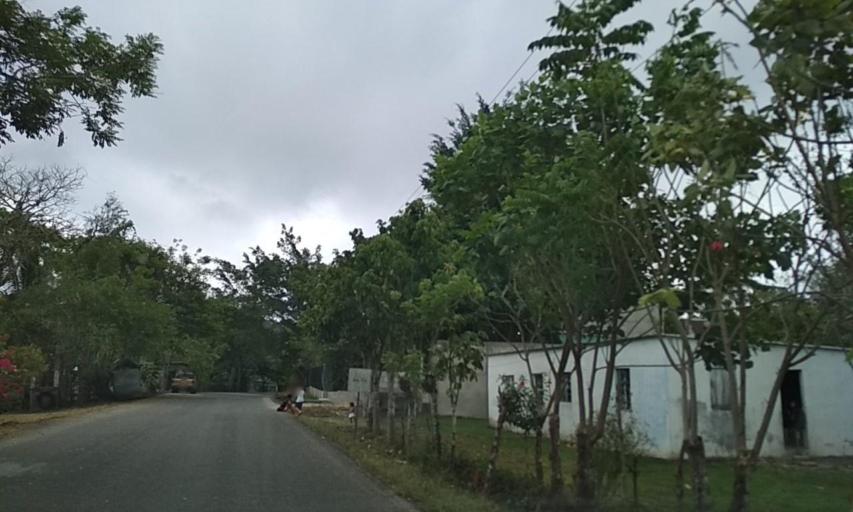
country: MX
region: Tabasco
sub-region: Huimanguillo
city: Francisco Rueda
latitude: 17.5781
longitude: -94.0981
